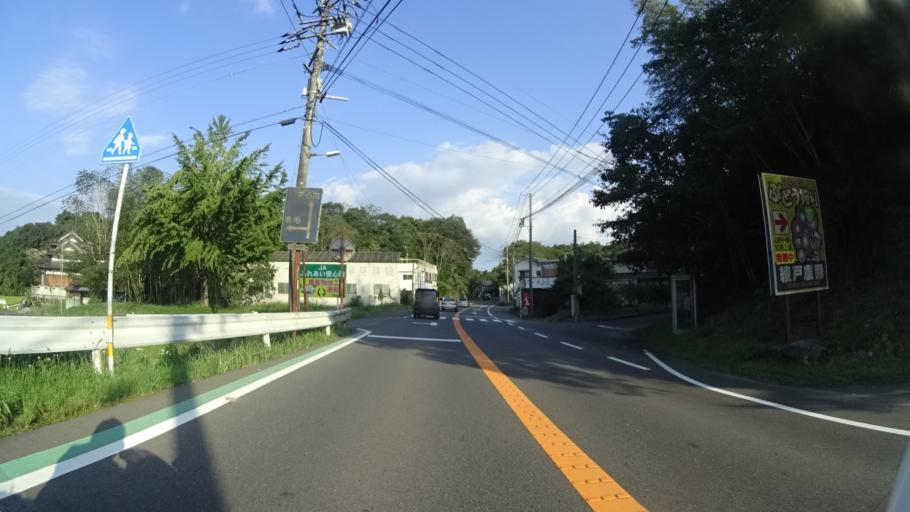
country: JP
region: Oita
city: Bungo-Takada-shi
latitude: 33.4447
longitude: 131.3439
